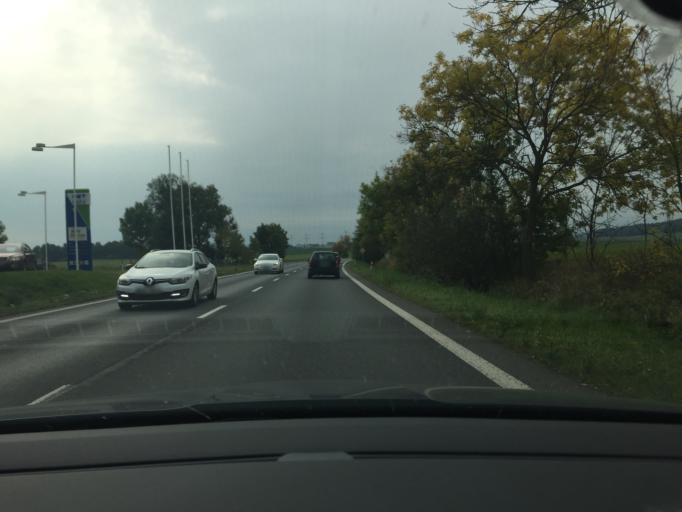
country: CZ
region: Jihocesky
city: Mirovice
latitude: 49.5371
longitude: 14.0809
